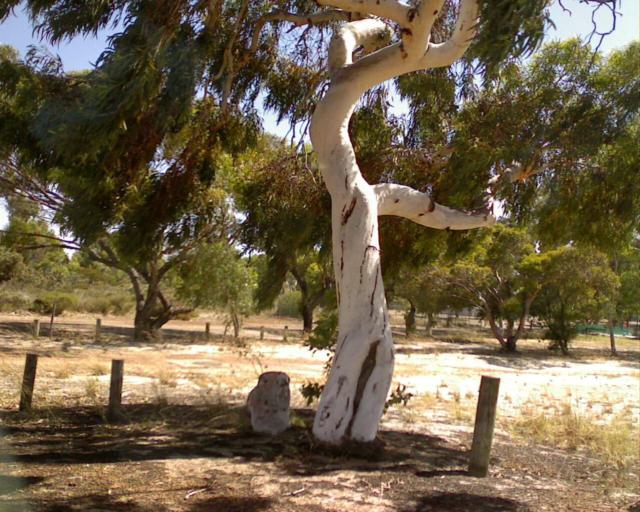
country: AU
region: Western Australia
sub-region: Dandaragan
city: Jurien Bay
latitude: -29.8198
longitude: 115.2668
